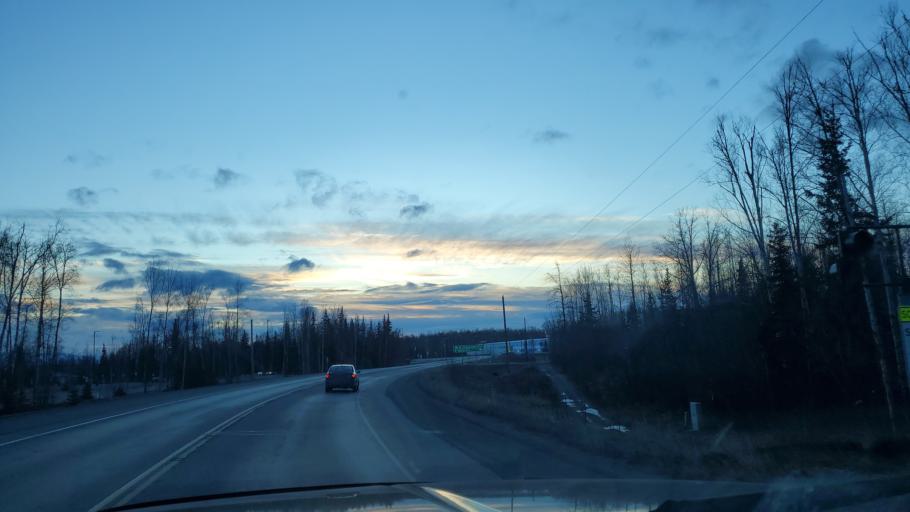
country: US
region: Alaska
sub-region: Matanuska-Susitna Borough
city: Wasilla
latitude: 61.5915
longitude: -149.4393
